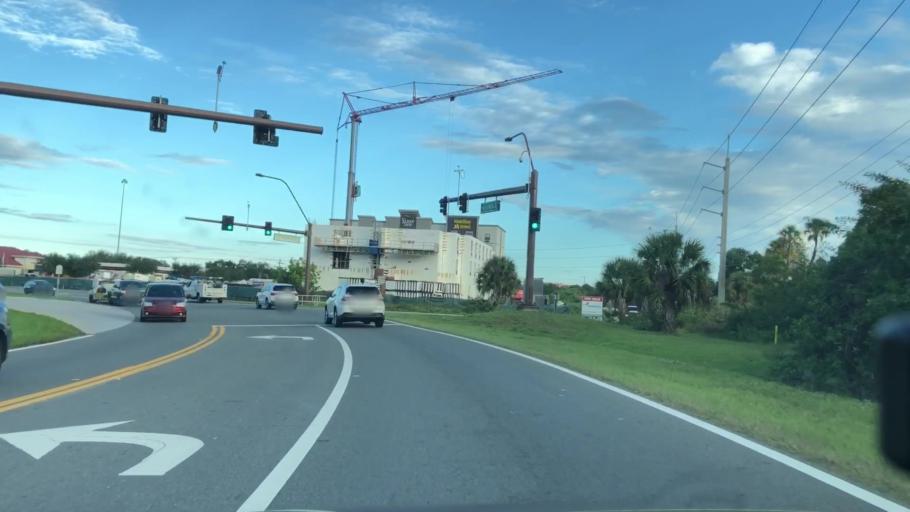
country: US
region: Florida
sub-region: Sarasota County
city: Fruitville
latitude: 27.3356
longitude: -82.4493
